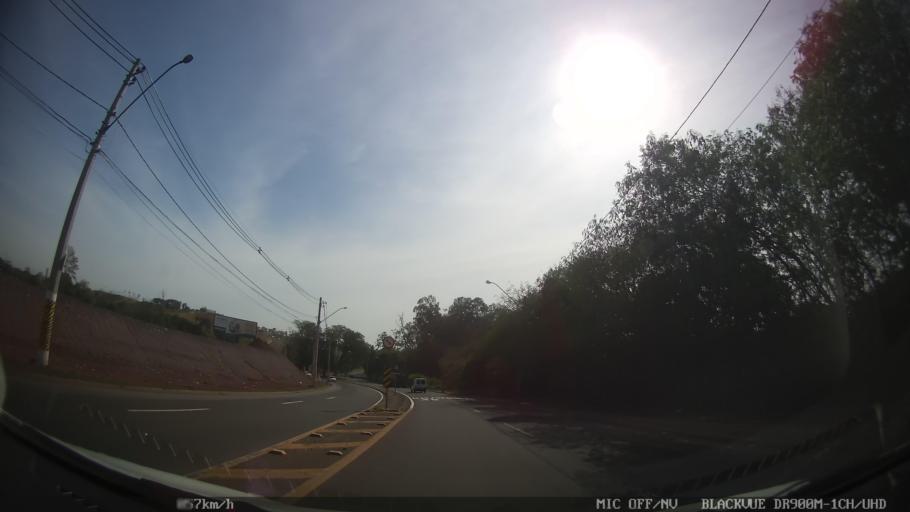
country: BR
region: Sao Paulo
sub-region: Piracicaba
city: Piracicaba
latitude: -22.7091
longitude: -47.6771
